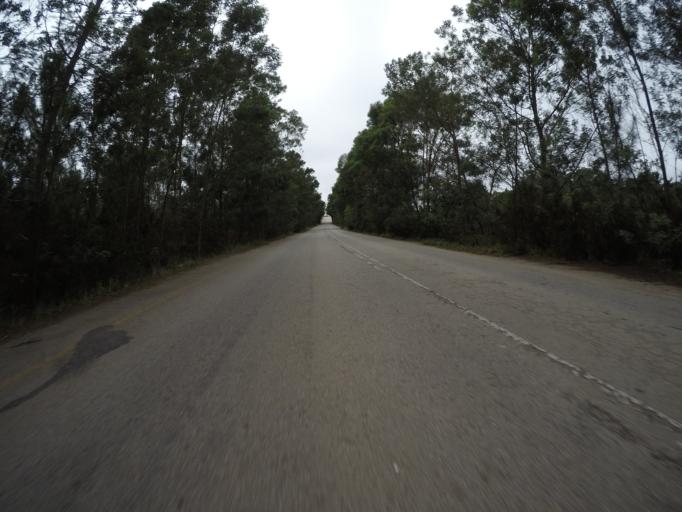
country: ZA
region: Eastern Cape
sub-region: Cacadu District Municipality
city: Kareedouw
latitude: -33.9966
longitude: 24.1592
